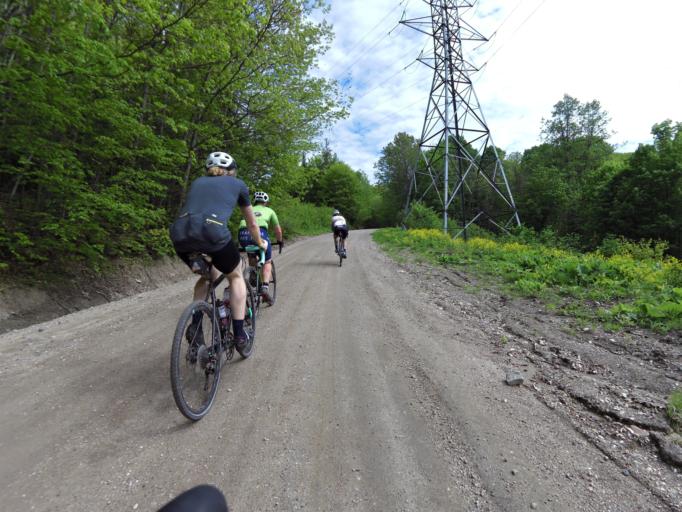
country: CA
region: Quebec
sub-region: Outaouais
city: Wakefield
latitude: 45.7855
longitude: -75.9136
